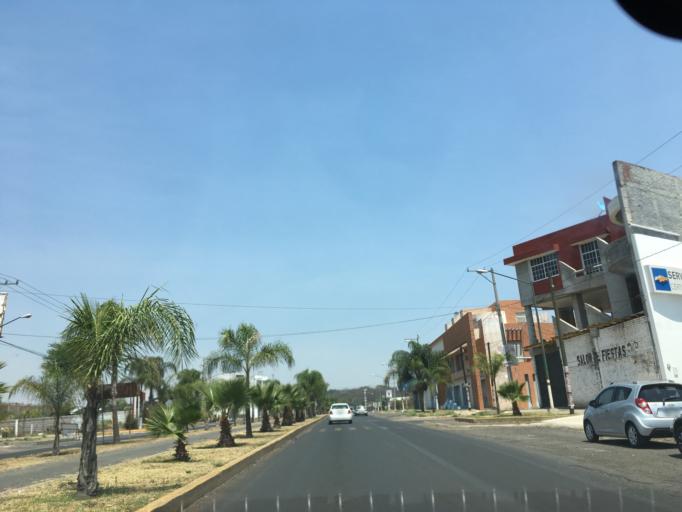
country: MX
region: Guanajuato
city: Moroleon
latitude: 20.1043
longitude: -101.1660
